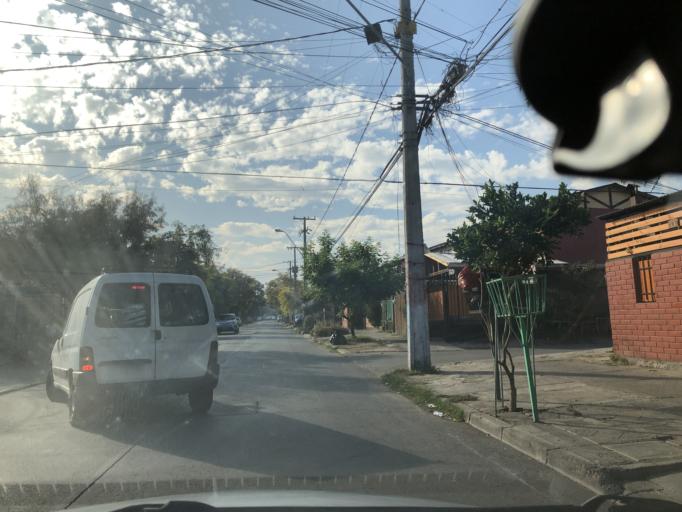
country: CL
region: Santiago Metropolitan
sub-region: Provincia de Cordillera
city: Puente Alto
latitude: -33.5898
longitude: -70.5662
